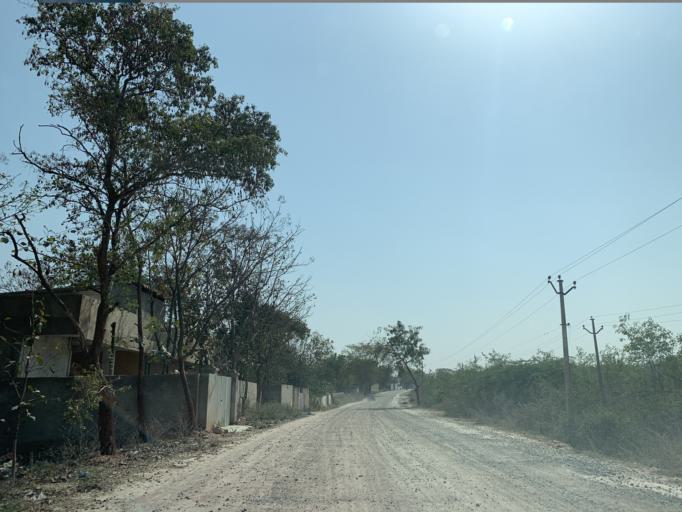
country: IN
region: Telangana
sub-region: Rangareddi
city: Sriramnagar
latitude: 17.3296
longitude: 78.2962
